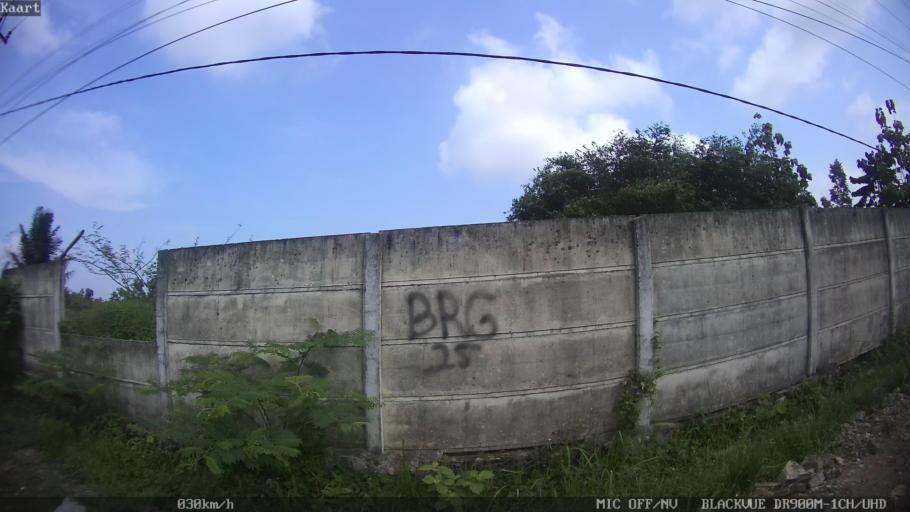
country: ID
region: Lampung
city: Kedaton
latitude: -5.3364
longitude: 105.2774
